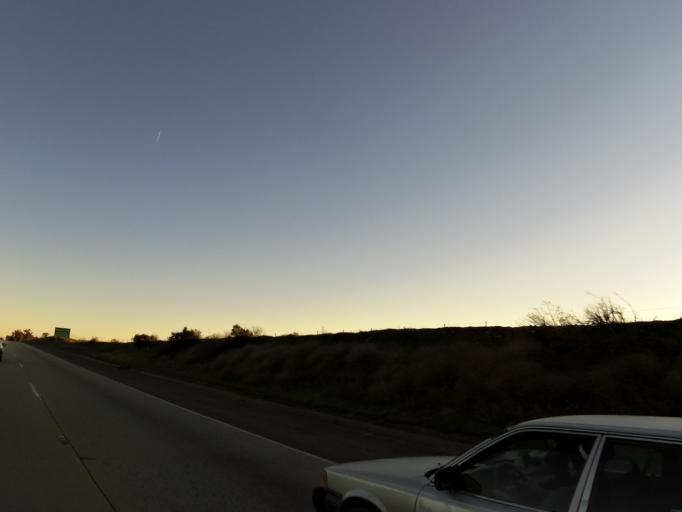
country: US
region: California
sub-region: Monterey County
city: Greenfield
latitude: 36.3476
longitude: -121.2630
